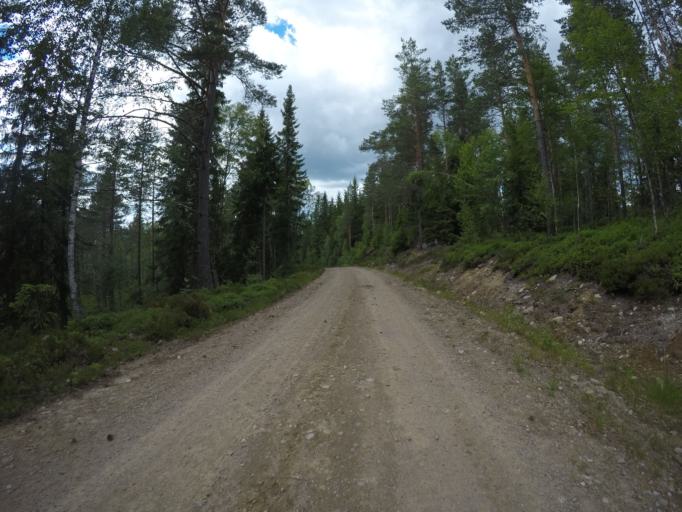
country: SE
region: Vaermland
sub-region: Filipstads Kommun
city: Lesjofors
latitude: 60.0725
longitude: 14.4521
